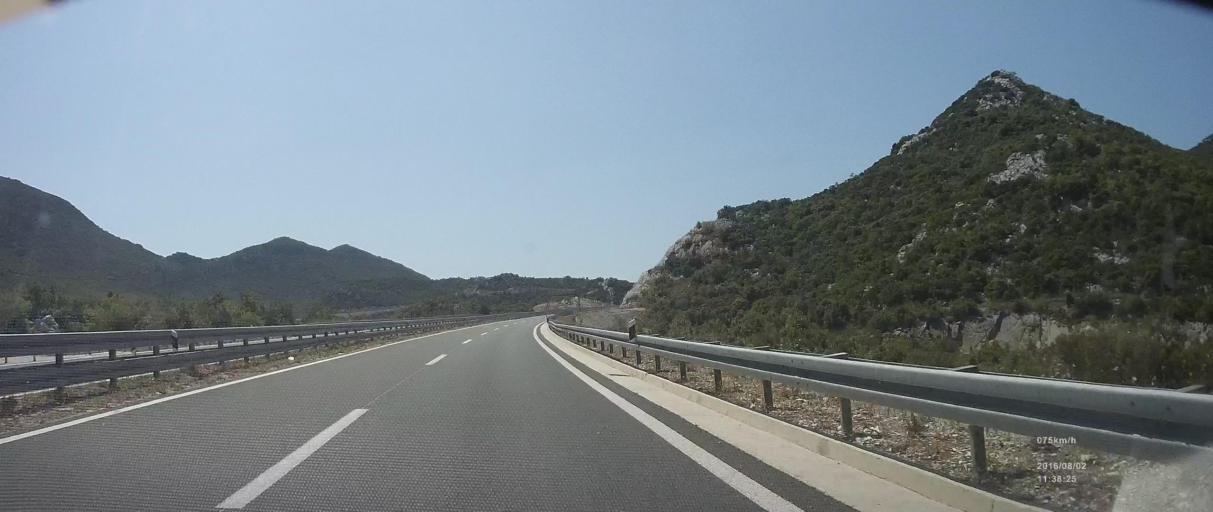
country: HR
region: Dubrovacko-Neretvanska
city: Komin
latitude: 43.0962
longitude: 17.4906
